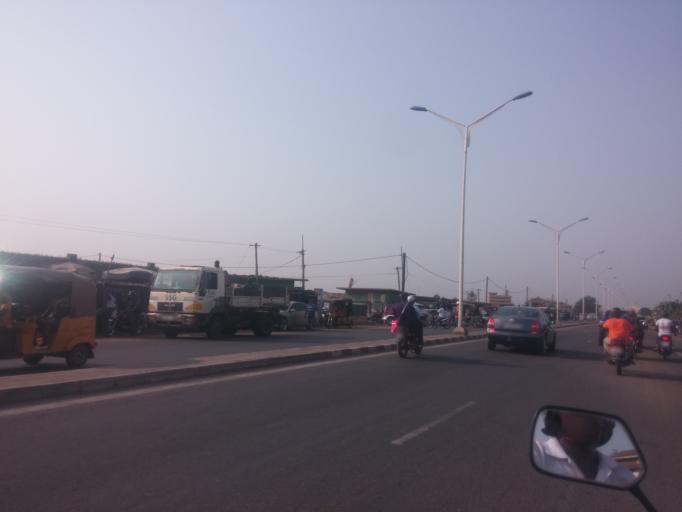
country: TG
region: Maritime
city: Lome
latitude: 6.1535
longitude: 1.2862
